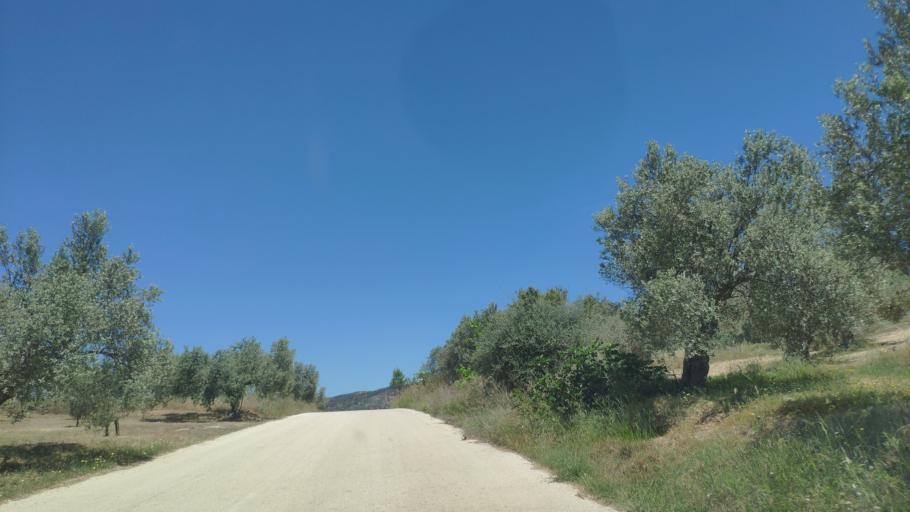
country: GR
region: Peloponnese
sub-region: Nomos Korinthias
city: Athikia
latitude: 37.8313
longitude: 22.9282
